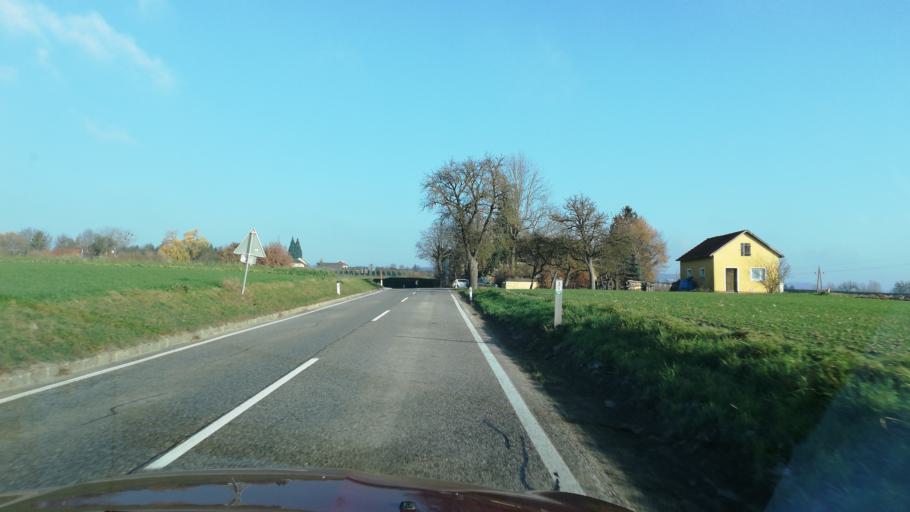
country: AT
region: Upper Austria
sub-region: Wels-Land
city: Buchkirchen
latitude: 48.2139
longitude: 14.0379
